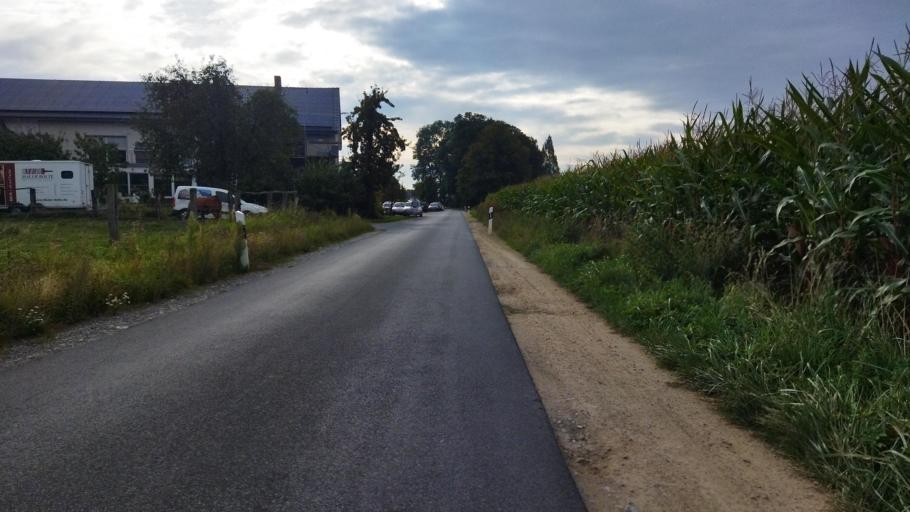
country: DE
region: Lower Saxony
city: Bad Laer
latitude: 52.0867
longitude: 8.1087
